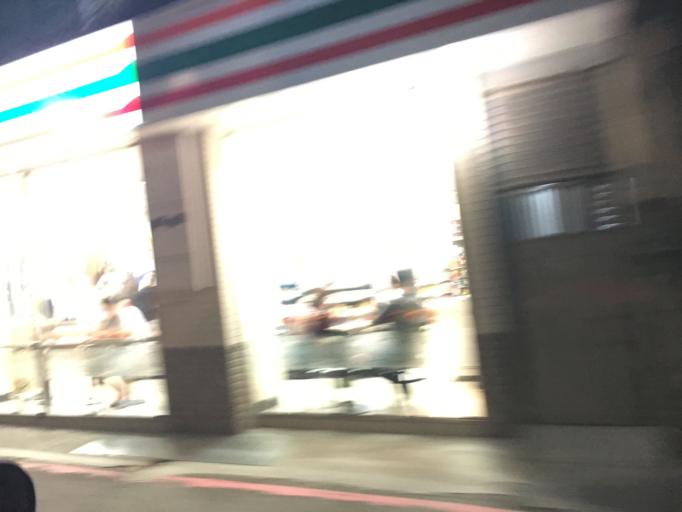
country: TW
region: Taiwan
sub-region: Hsinchu
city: Hsinchu
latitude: 24.8031
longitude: 120.9834
